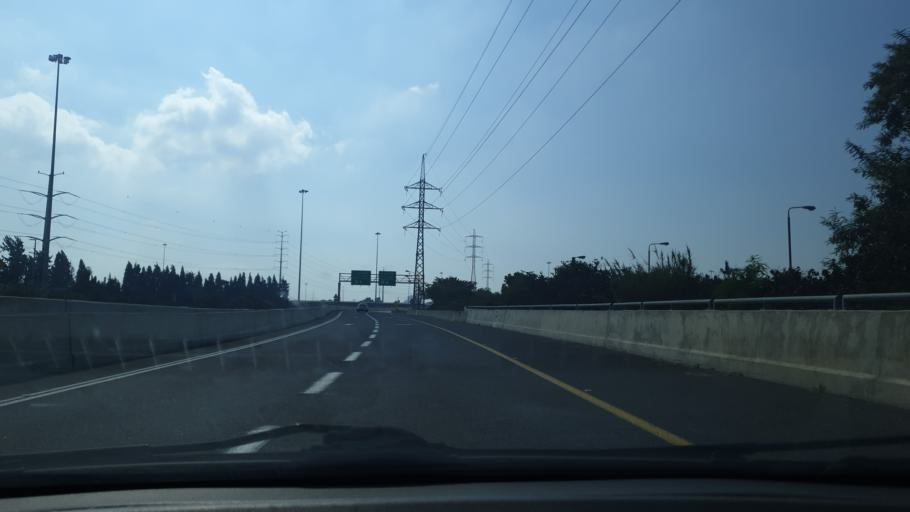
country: IL
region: Central District
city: Bet Dagan
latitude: 32.0033
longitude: 34.8077
